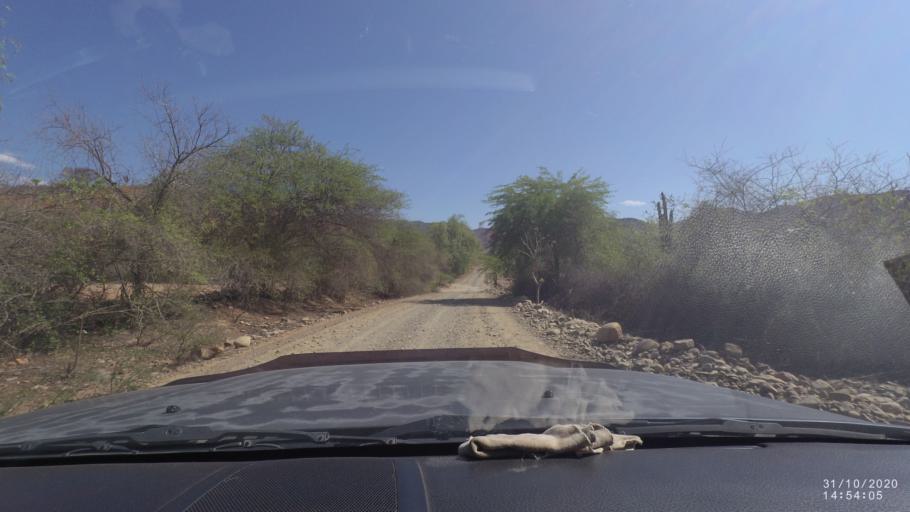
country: BO
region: Cochabamba
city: Aiquile
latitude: -18.2236
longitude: -64.8571
